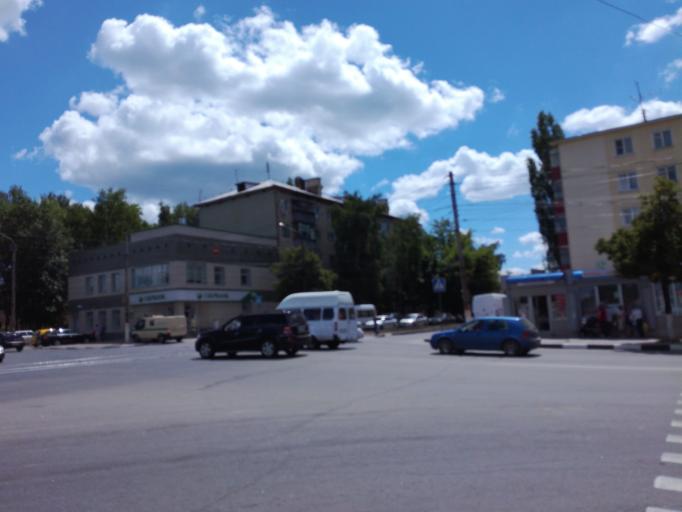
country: RU
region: Kursk
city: Kursk
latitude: 51.7468
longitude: 36.2467
